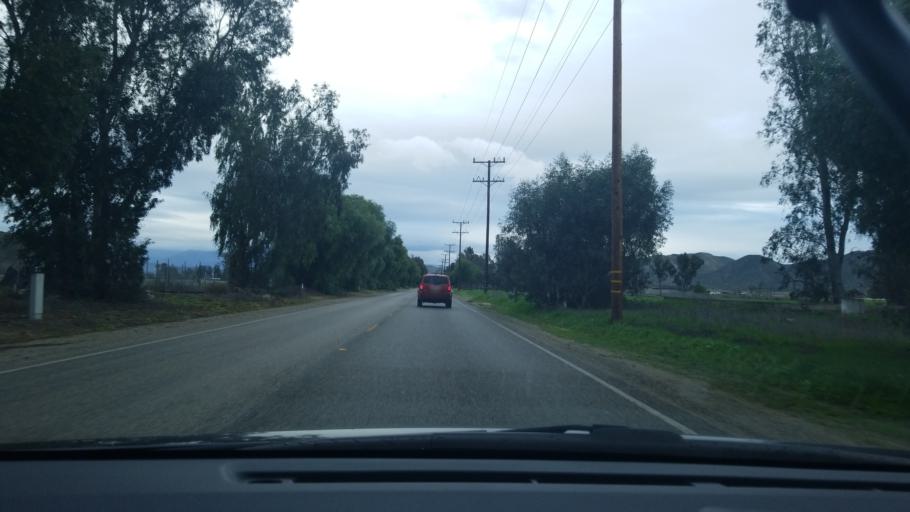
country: US
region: California
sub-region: Riverside County
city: Winchester
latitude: 33.7074
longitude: -117.0637
